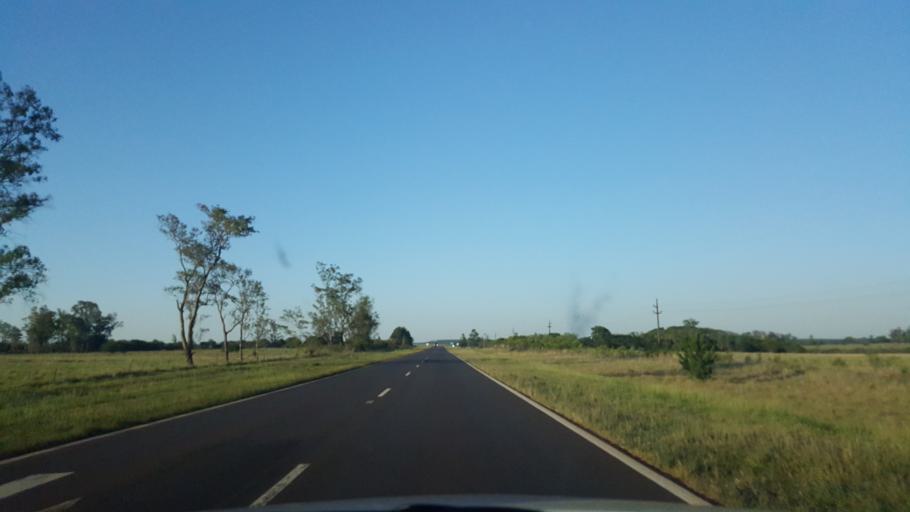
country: AR
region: Corrientes
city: Santo Tome
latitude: -28.4837
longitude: -56.1148
